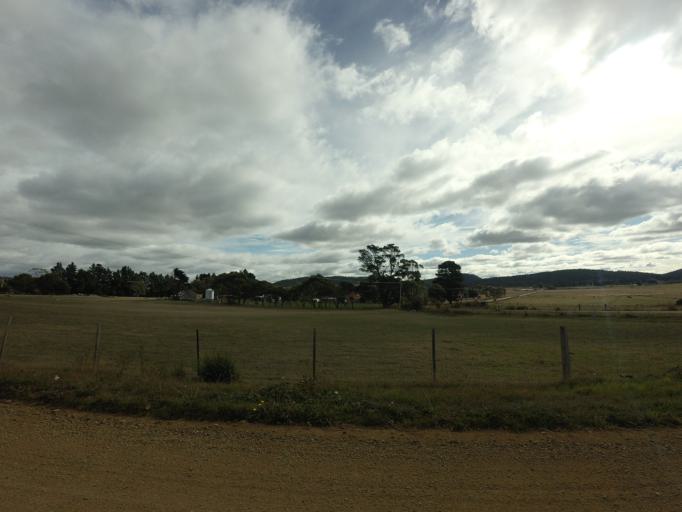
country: AU
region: Tasmania
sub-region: Brighton
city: Bridgewater
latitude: -42.4131
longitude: 147.3989
